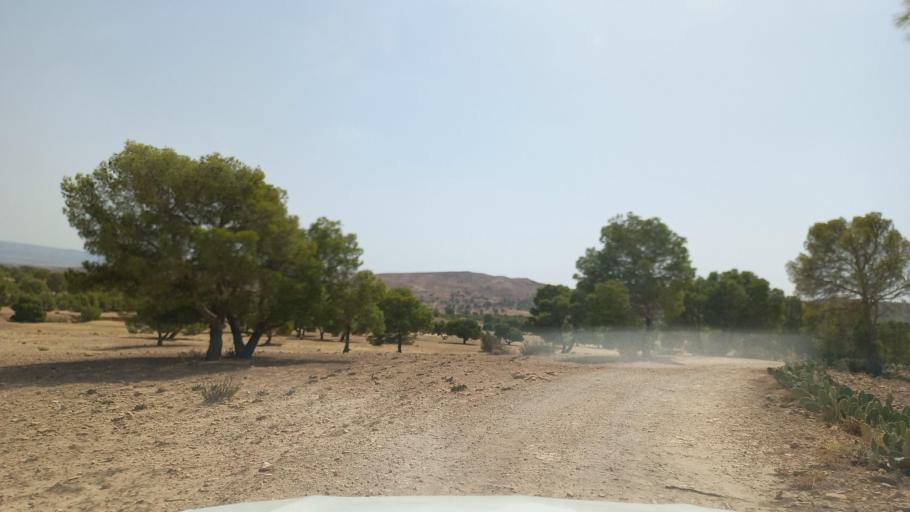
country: TN
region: Al Qasrayn
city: Sbiba
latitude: 35.3981
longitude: 8.9859
